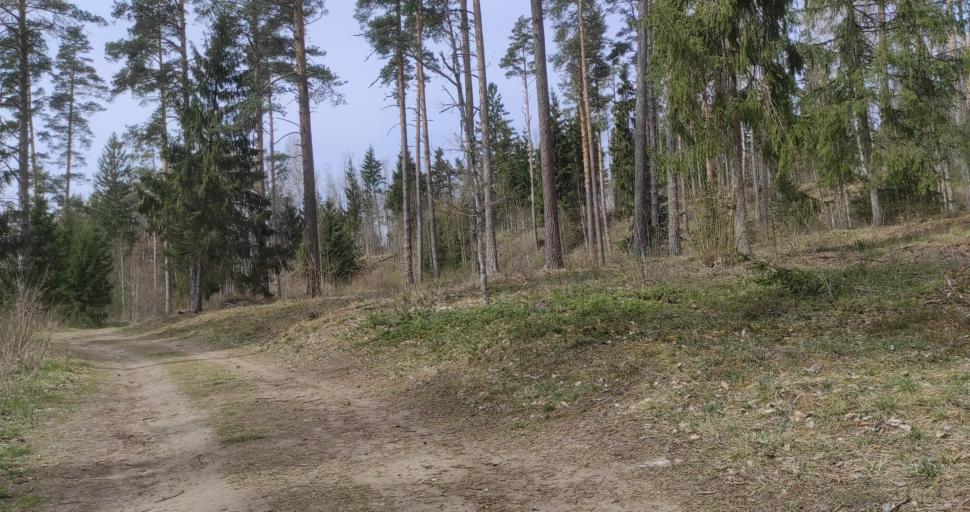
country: LV
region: Talsu Rajons
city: Stende
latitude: 57.0824
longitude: 22.3767
